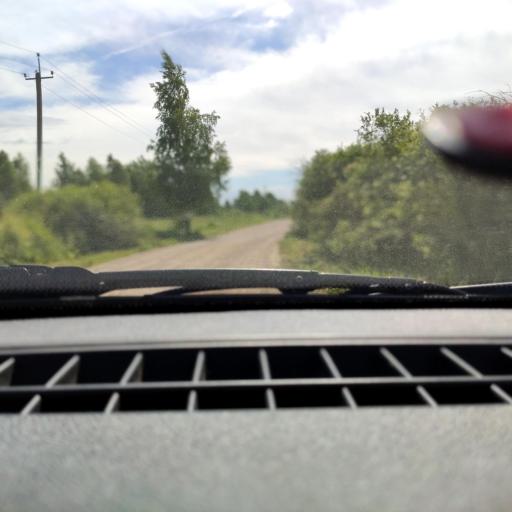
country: RU
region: Bashkortostan
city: Kabakovo
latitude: 54.7300
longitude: 56.2012
